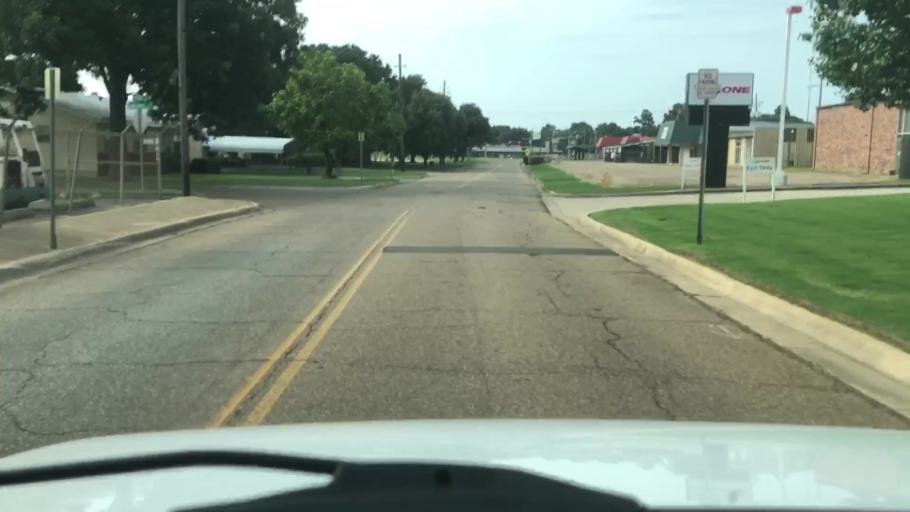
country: US
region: Texas
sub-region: Bowie County
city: Wake Village
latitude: 33.4393
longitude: -94.0826
